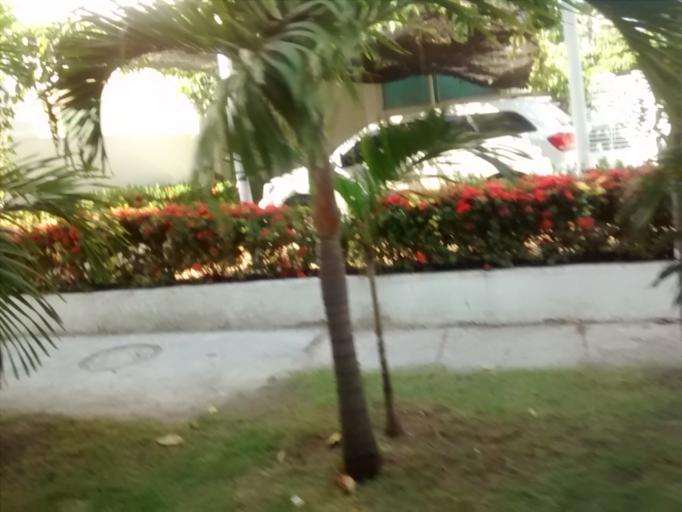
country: CO
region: Bolivar
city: Cartagena
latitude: 10.3931
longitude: -75.5493
